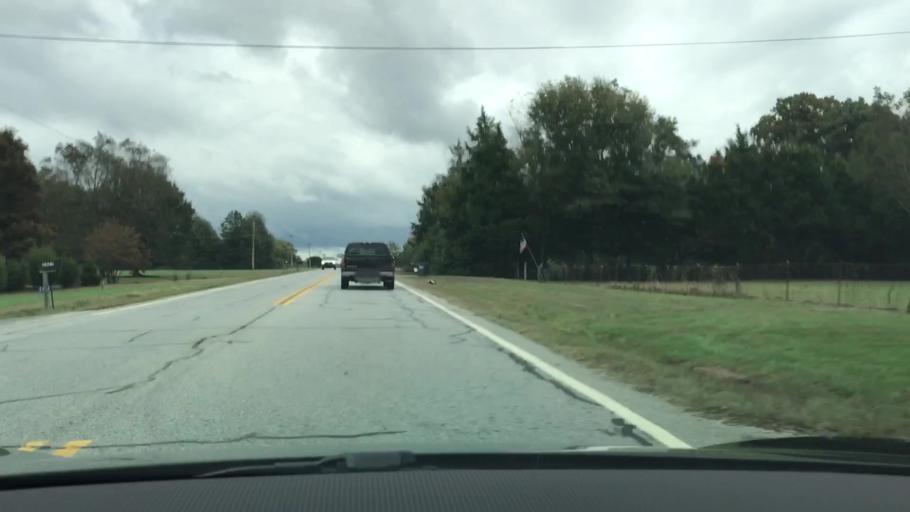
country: US
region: Georgia
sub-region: Oconee County
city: Watkinsville
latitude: 33.8317
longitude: -83.3782
